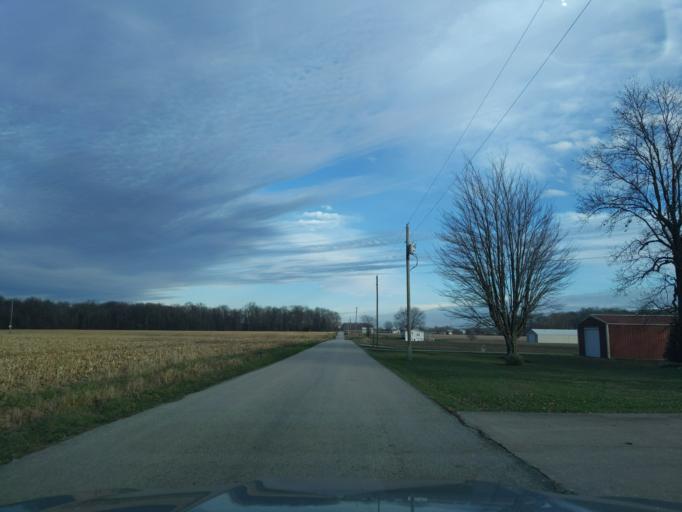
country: US
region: Indiana
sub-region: Decatur County
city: Westport
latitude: 39.2193
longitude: -85.4956
